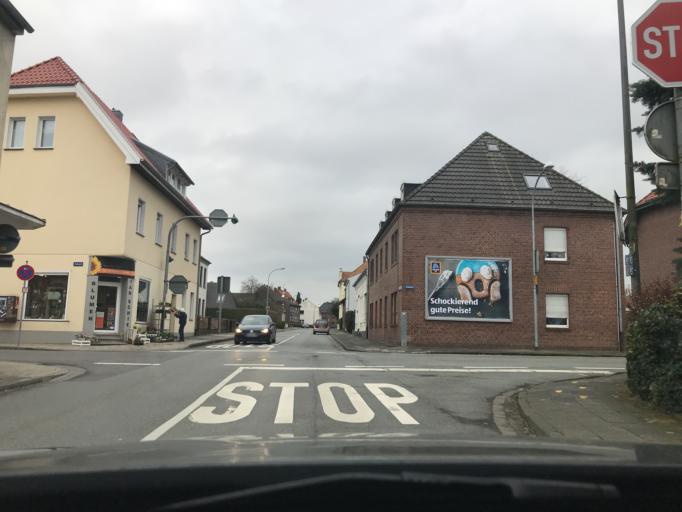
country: DE
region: North Rhine-Westphalia
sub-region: Regierungsbezirk Dusseldorf
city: Uedem
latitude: 51.6670
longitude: 6.2744
